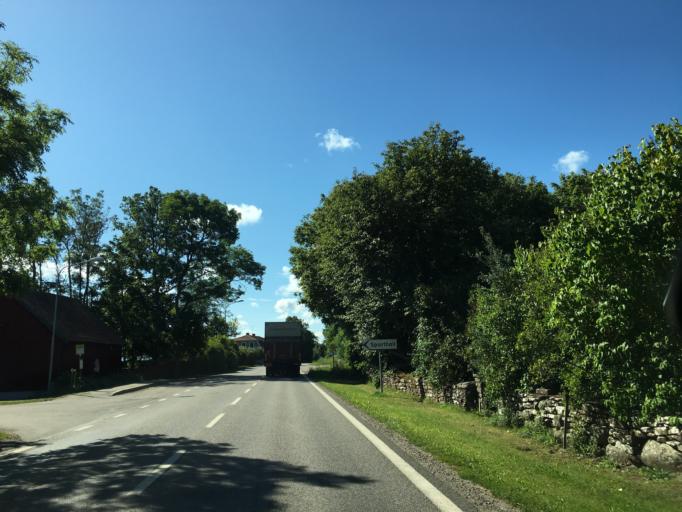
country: SE
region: Kalmar
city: Faerjestaden
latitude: 56.6369
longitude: 16.5161
